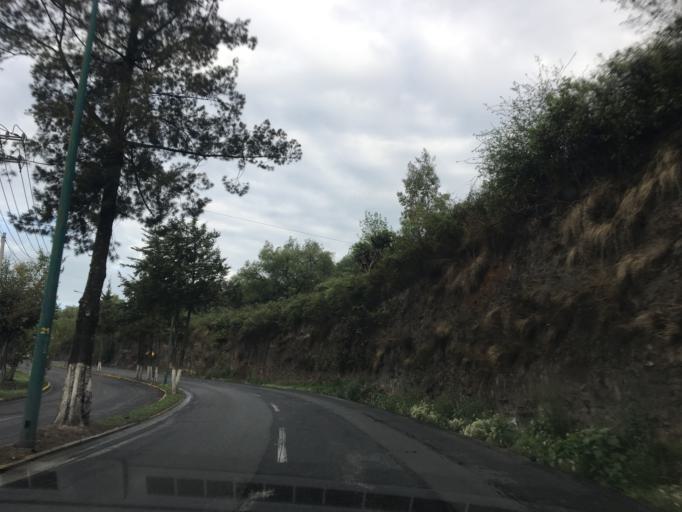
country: MX
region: Mexico
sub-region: Naucalpan de Juarez
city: Rincon Verde
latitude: 19.5330
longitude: -99.2619
